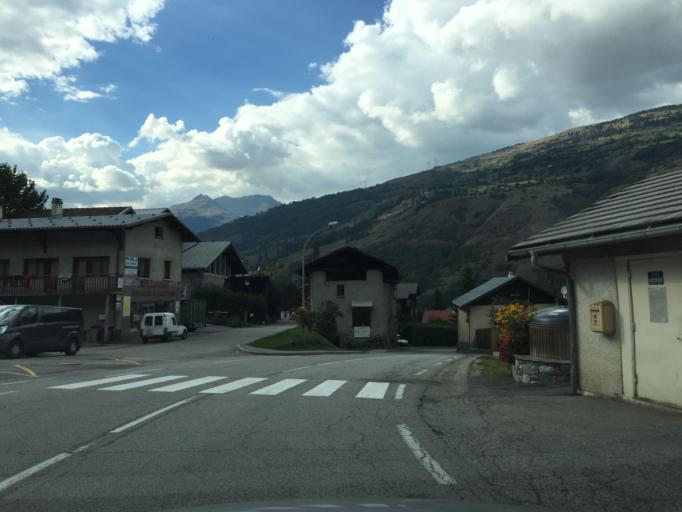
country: FR
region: Rhone-Alpes
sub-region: Departement de la Savoie
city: Bourg-Saint-Maurice
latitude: 45.5696
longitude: 6.7408
